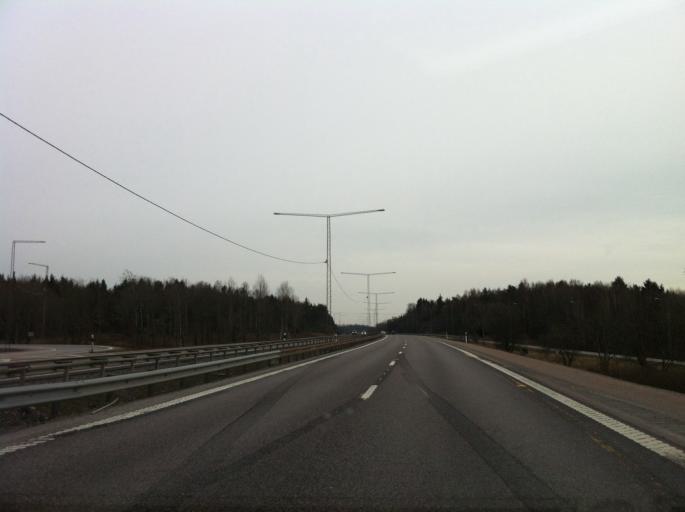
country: SE
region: Vaestra Goetaland
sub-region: Stenungsunds Kommun
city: Stora Hoga
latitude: 57.9752
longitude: 11.8398
